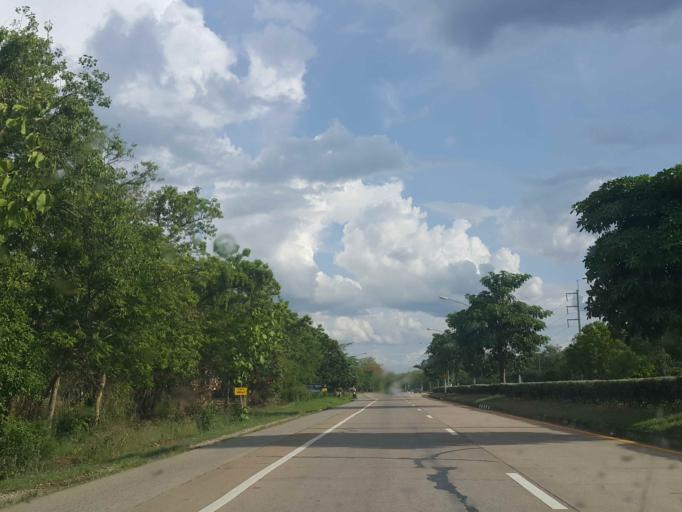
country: TH
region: Phrae
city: Sung Men
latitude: 18.0066
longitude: 100.1049
